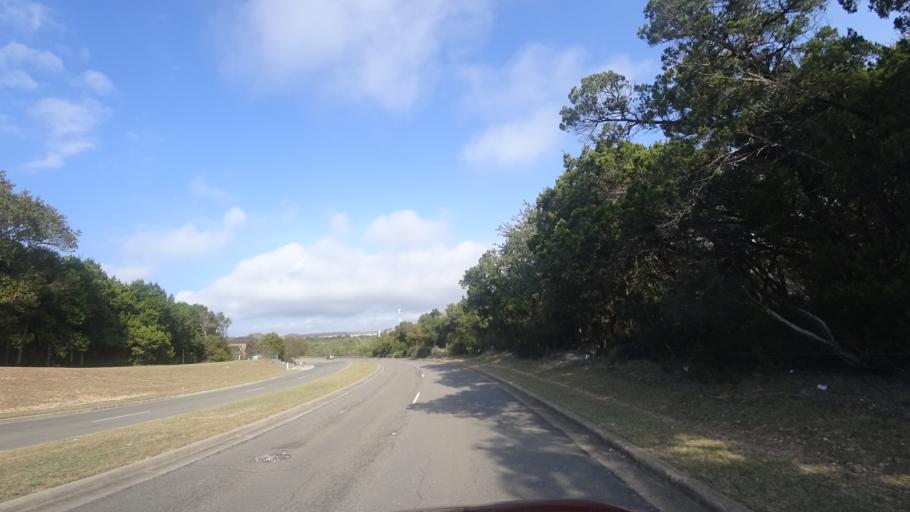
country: US
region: Texas
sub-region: Williamson County
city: Anderson Mill
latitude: 30.4028
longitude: -97.8461
